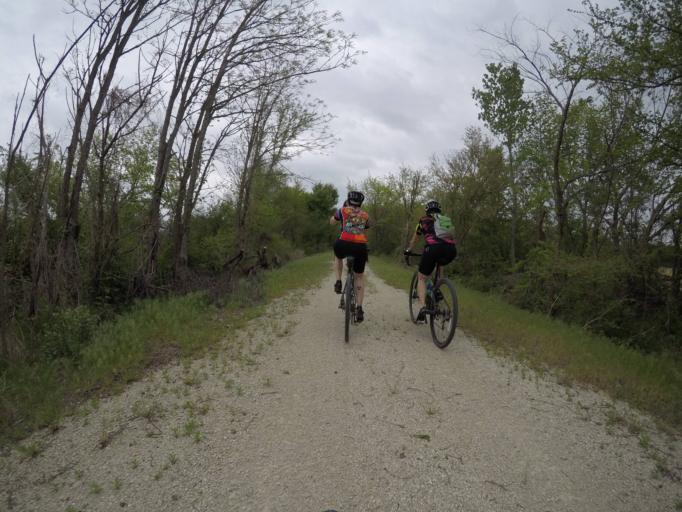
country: US
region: Nebraska
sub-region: Gage County
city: Wymore
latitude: 40.1746
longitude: -96.6547
